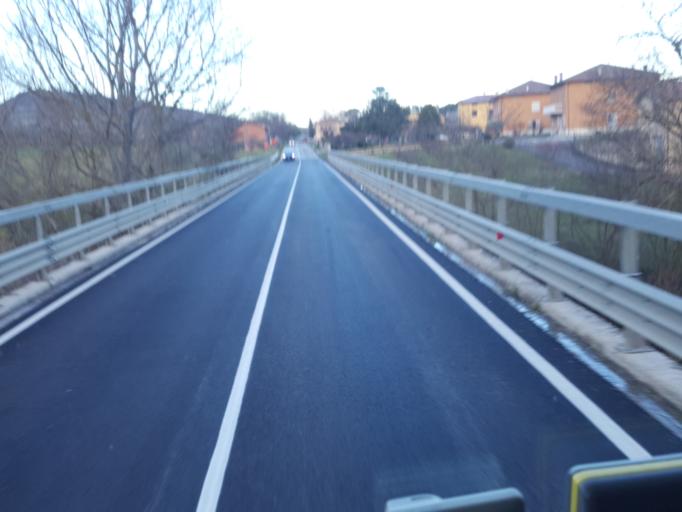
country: IT
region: The Marches
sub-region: Provincia di Macerata
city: San Severino Marche
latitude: 43.2439
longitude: 13.2229
